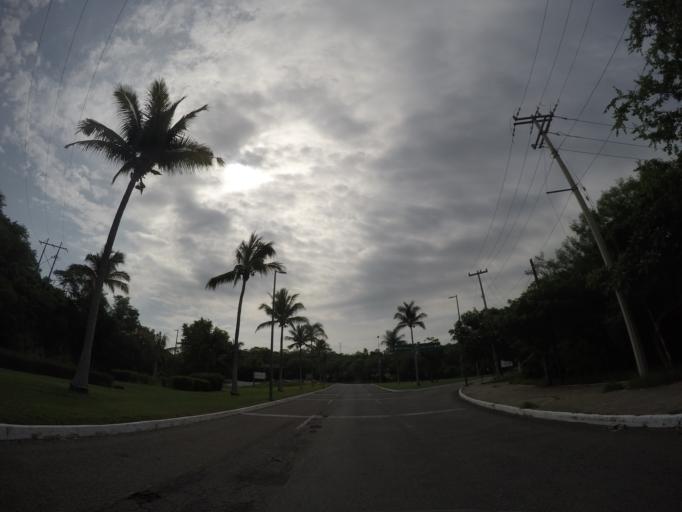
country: MX
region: Oaxaca
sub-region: Santa Maria Huatulco
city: Sector H Tres
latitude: 15.7819
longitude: -96.1562
